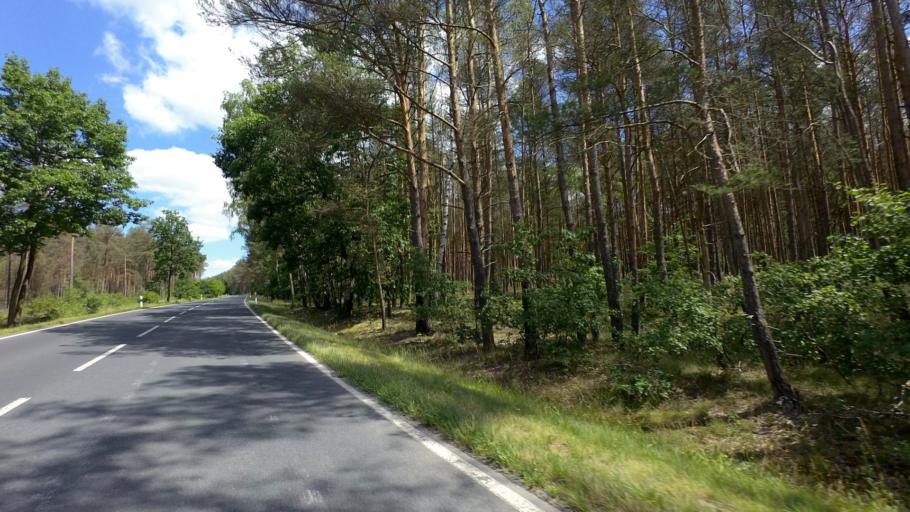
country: DE
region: Brandenburg
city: Sonnewalde
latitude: 51.7334
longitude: 13.6794
